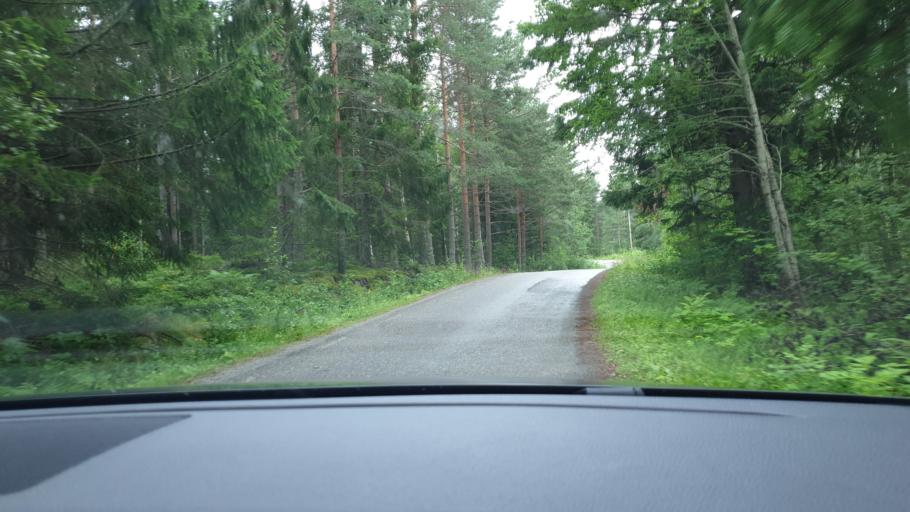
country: SE
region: Gaevleborg
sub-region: Hudiksvalls Kommun
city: Iggesund
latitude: 61.5373
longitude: 17.0106
